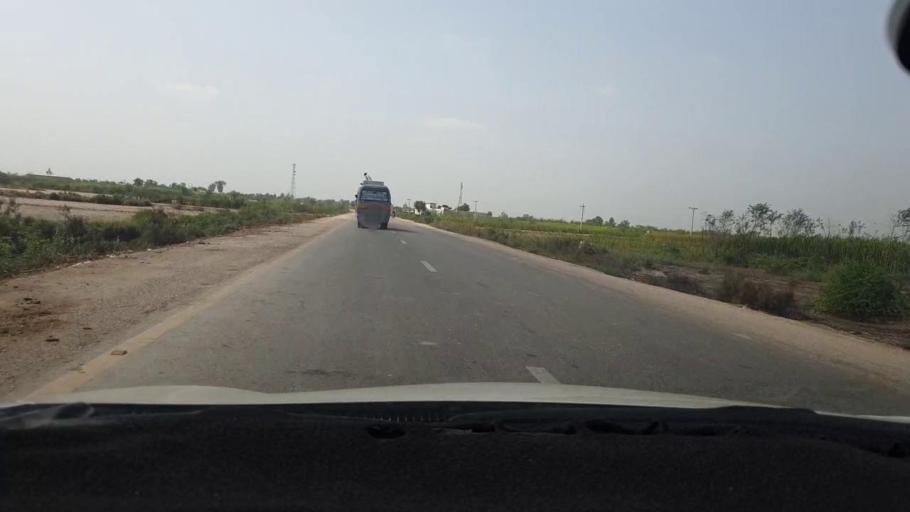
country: PK
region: Sindh
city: Mirpur Khas
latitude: 25.5782
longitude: 69.0709
